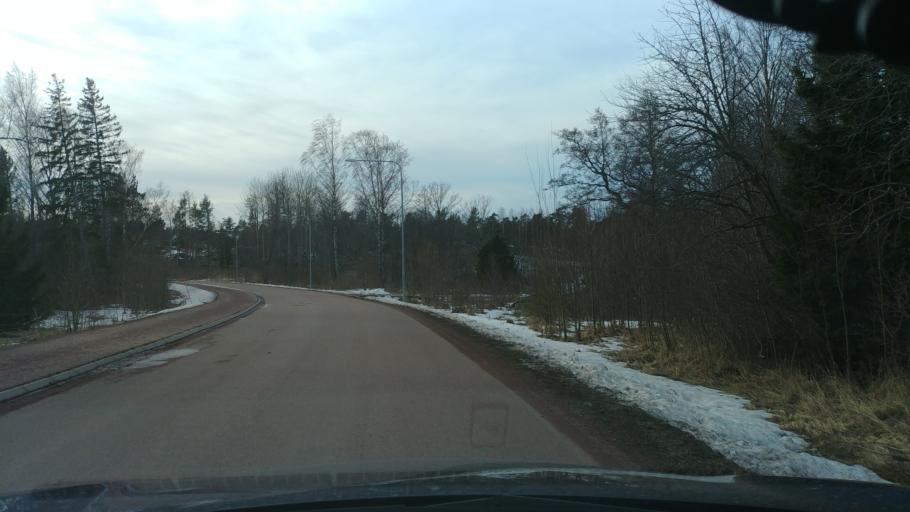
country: AX
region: Mariehamns stad
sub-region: Mariehamn
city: Mariehamn
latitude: 60.1046
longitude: 19.8954
